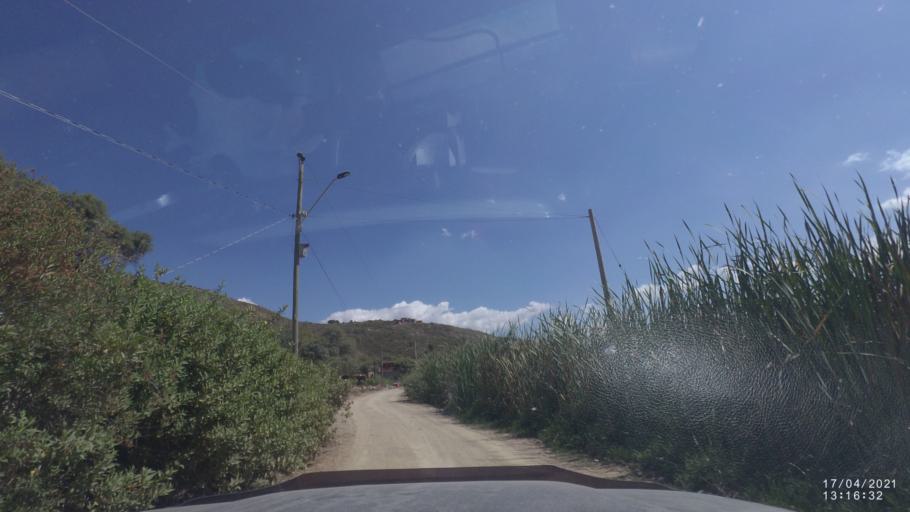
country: BO
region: Cochabamba
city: Cochabamba
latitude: -17.4166
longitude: -66.2374
